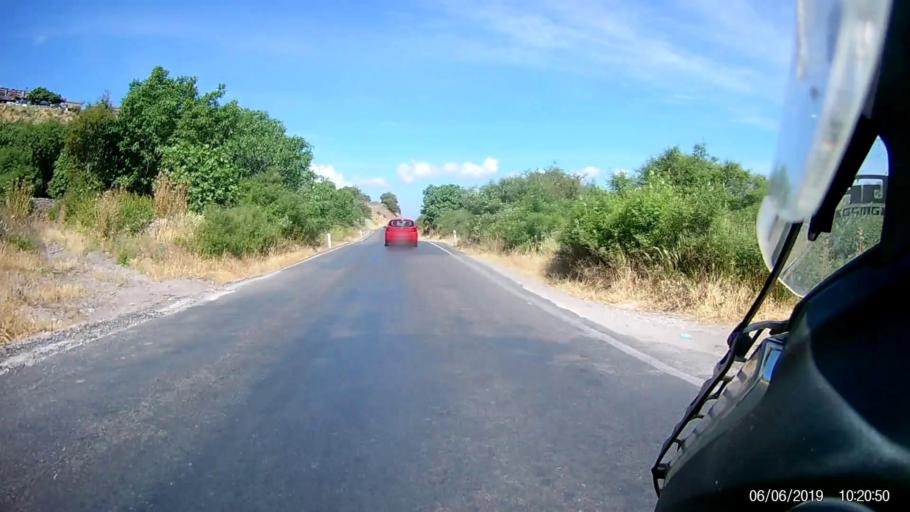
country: TR
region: Canakkale
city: Ayvacik
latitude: 39.5188
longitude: 26.4475
